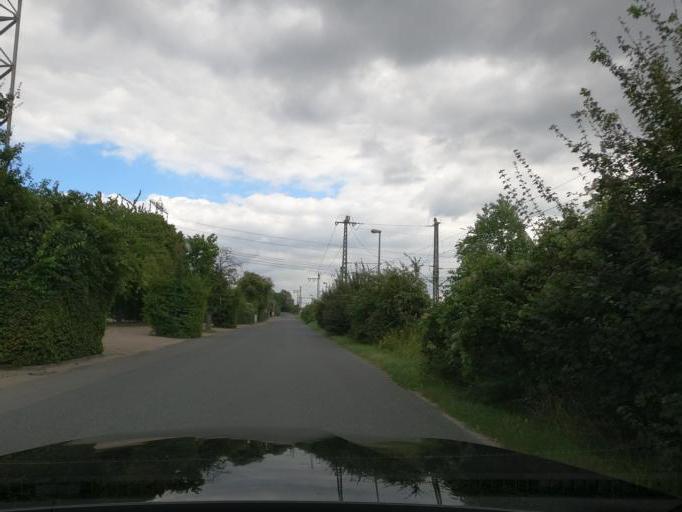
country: DE
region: Lower Saxony
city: Lehrte
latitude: 52.3773
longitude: 9.9179
